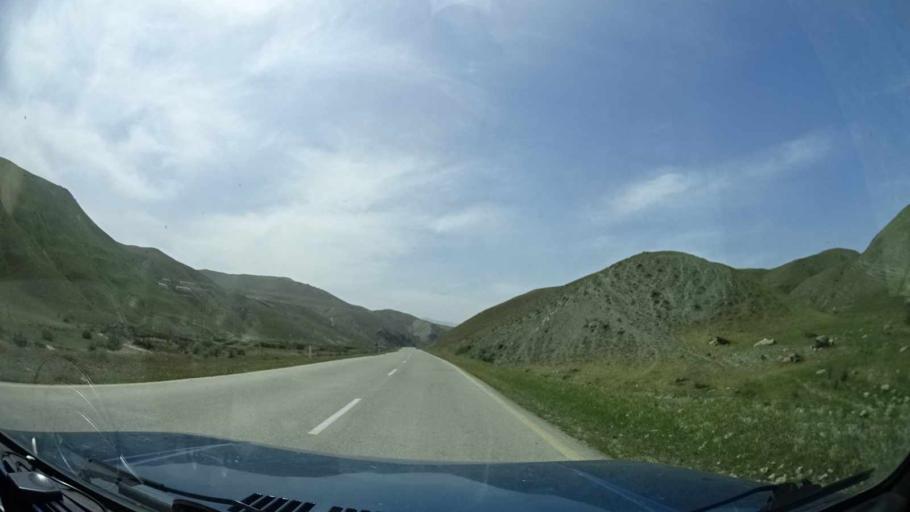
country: AZ
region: Xizi
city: Kilyazi
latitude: 40.8494
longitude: 49.2623
